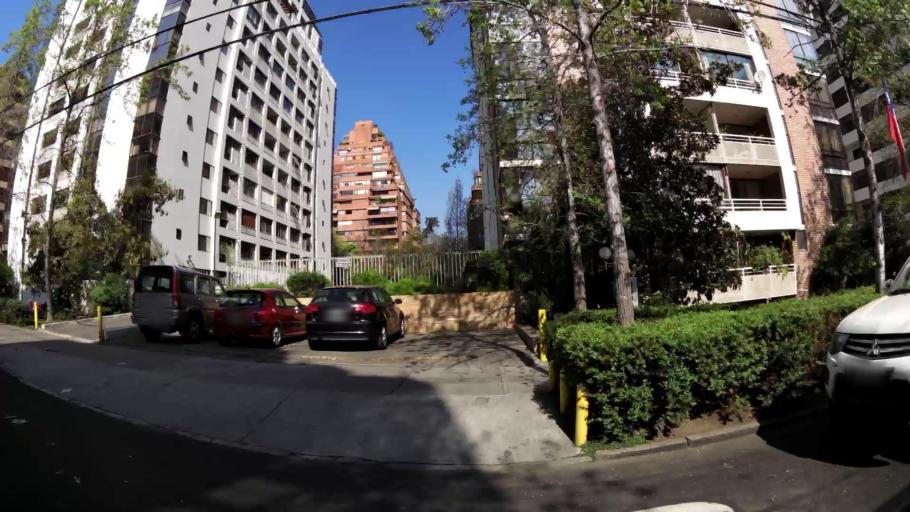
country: CL
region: Santiago Metropolitan
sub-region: Provincia de Santiago
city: Villa Presidente Frei, Nunoa, Santiago, Chile
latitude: -33.4056
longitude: -70.5959
